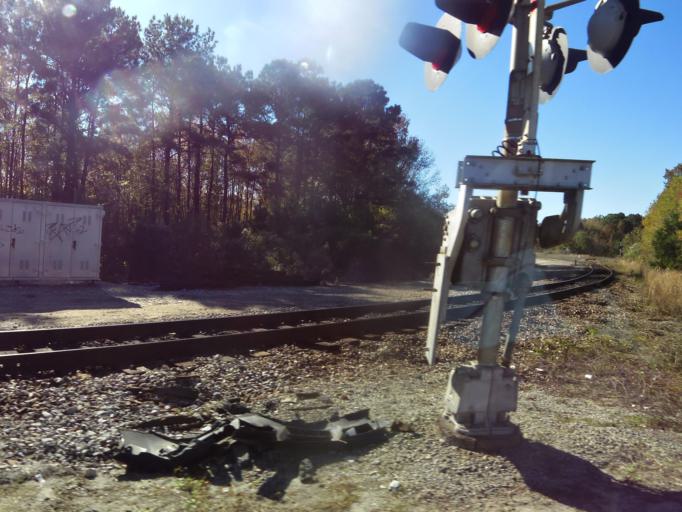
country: US
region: Georgia
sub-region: Chatham County
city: Garden City
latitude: 32.0742
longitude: -81.1427
